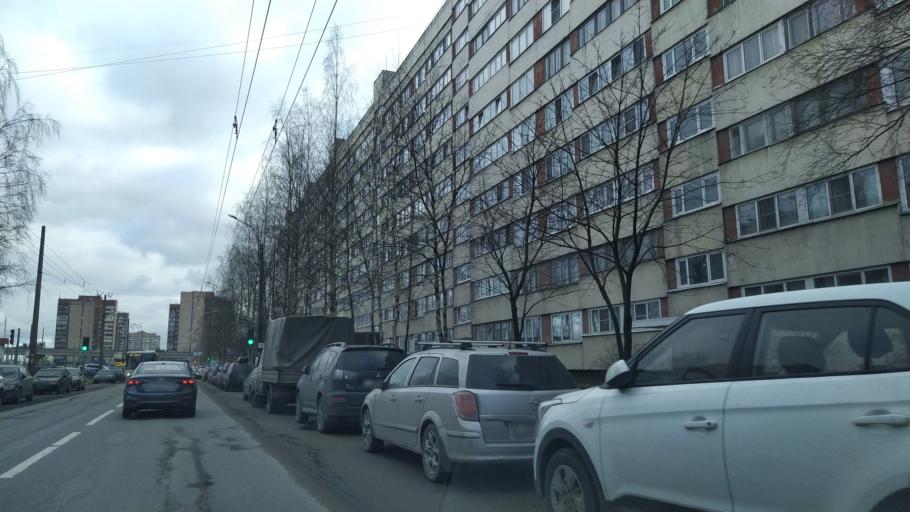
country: RU
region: Leningrad
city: Bugry
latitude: 60.0526
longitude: 30.3750
